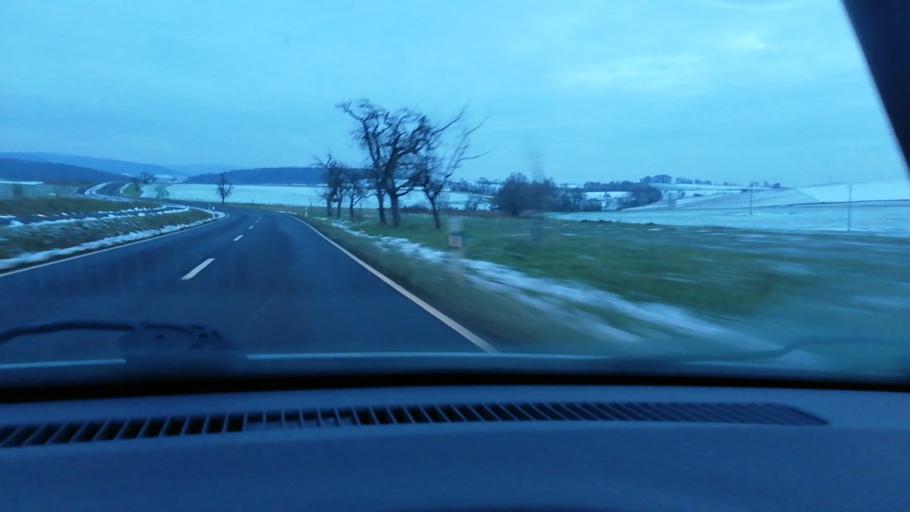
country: DE
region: Bavaria
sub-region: Regierungsbezirk Unterfranken
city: Geiselbach
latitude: 50.1166
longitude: 9.2045
